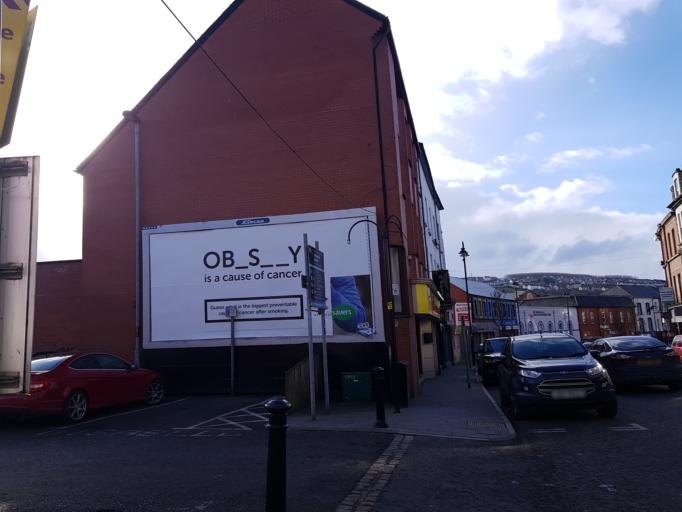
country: GB
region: Northern Ireland
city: Londonderry County Borough
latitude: 54.9933
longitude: -7.3195
